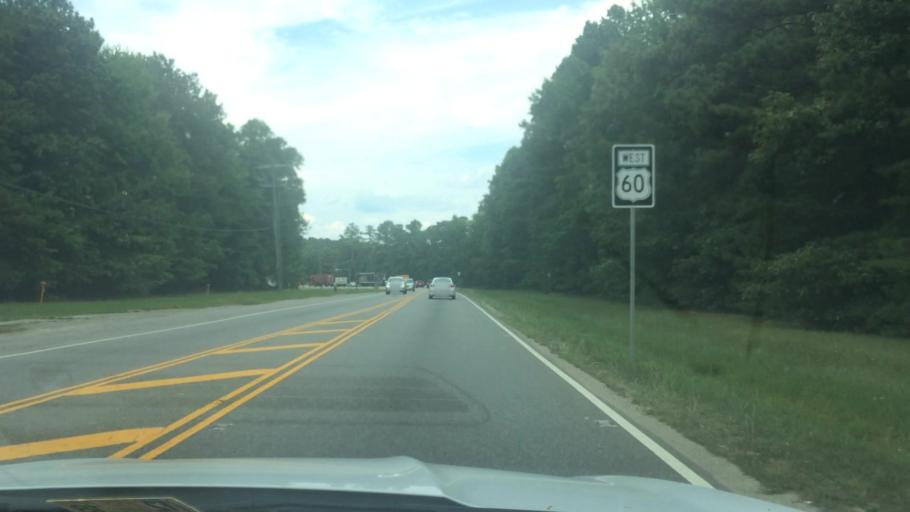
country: US
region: Virginia
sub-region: York County
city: Yorktown
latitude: 37.1781
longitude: -76.5697
